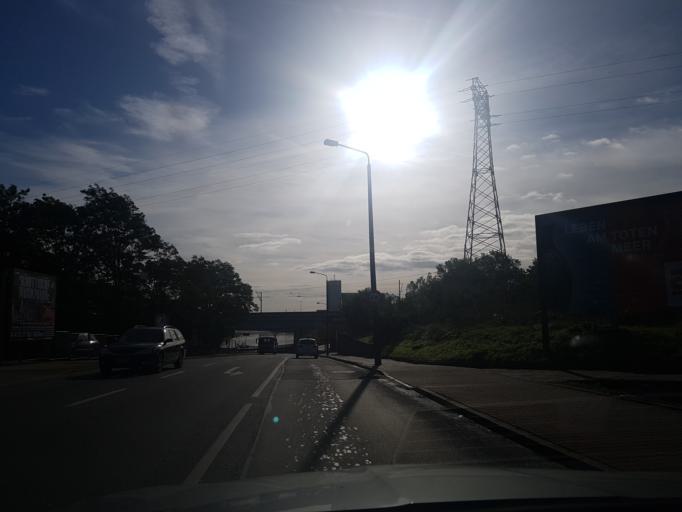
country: DE
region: Saxony
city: Riesa
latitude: 51.3117
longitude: 13.2916
